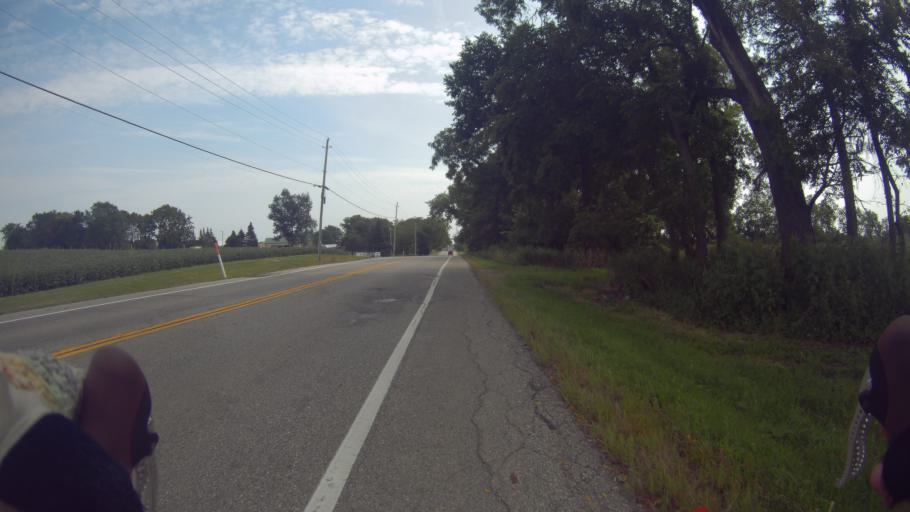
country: US
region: Wisconsin
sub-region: Dane County
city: Monona
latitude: 43.0992
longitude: -89.2782
